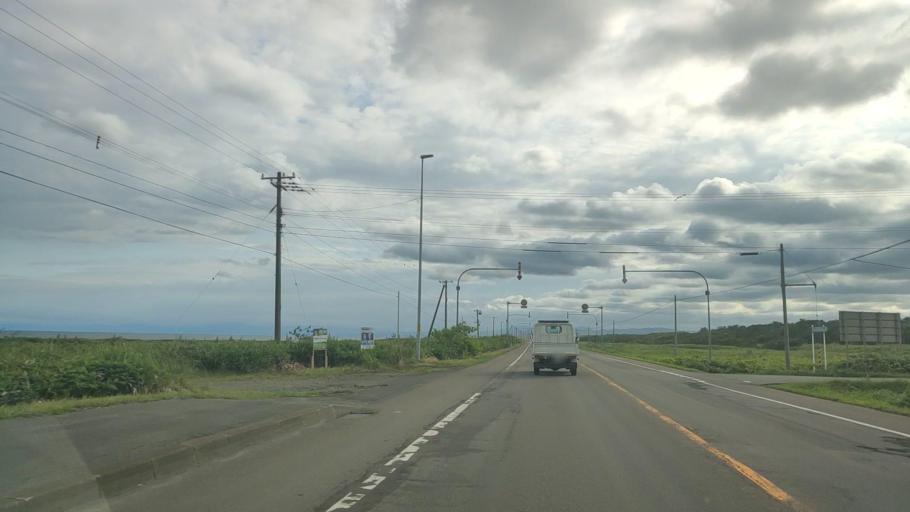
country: JP
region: Hokkaido
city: Niseko Town
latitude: 42.5756
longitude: 140.4503
